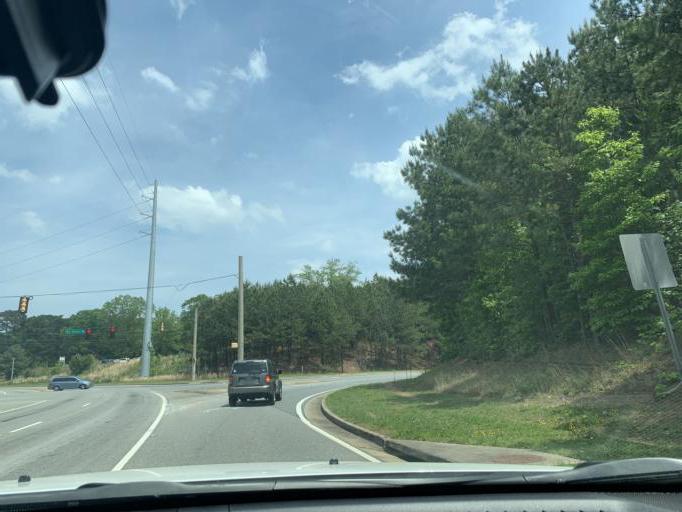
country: US
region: Georgia
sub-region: Forsyth County
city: Cumming
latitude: 34.1551
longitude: -84.1554
